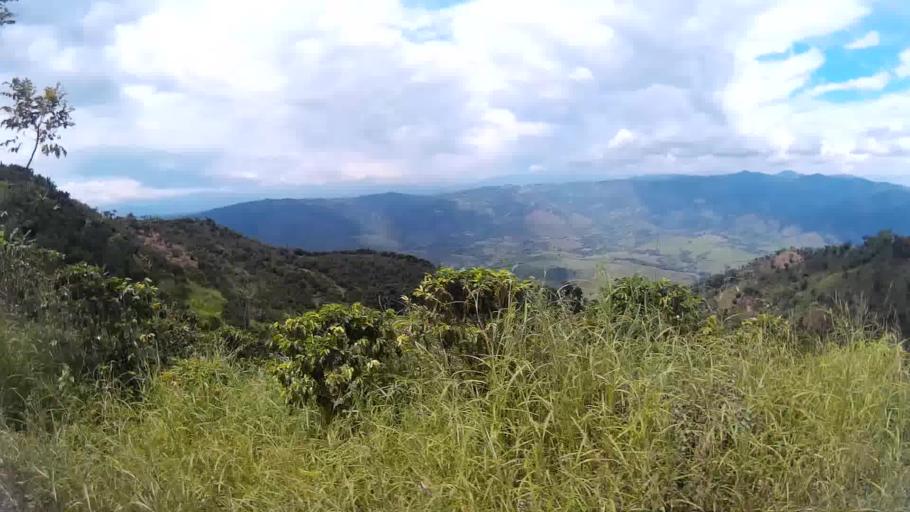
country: CO
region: Caldas
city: Belalcazar
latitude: 4.9770
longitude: -75.8174
